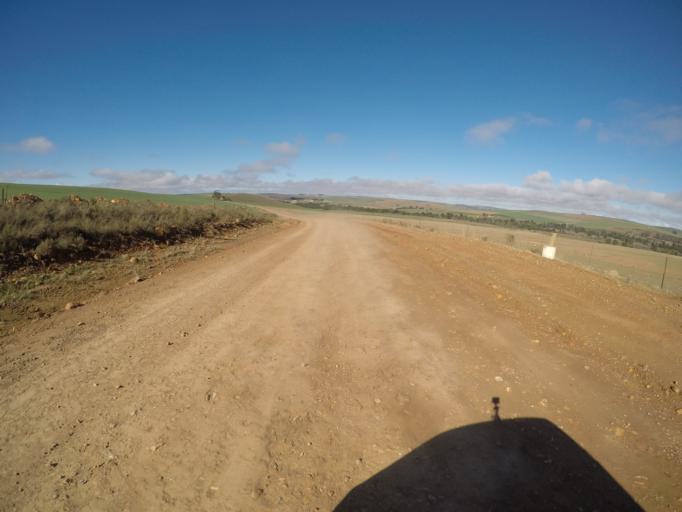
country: ZA
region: Western Cape
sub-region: Overberg District Municipality
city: Caledon
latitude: -34.1157
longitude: 19.7114
